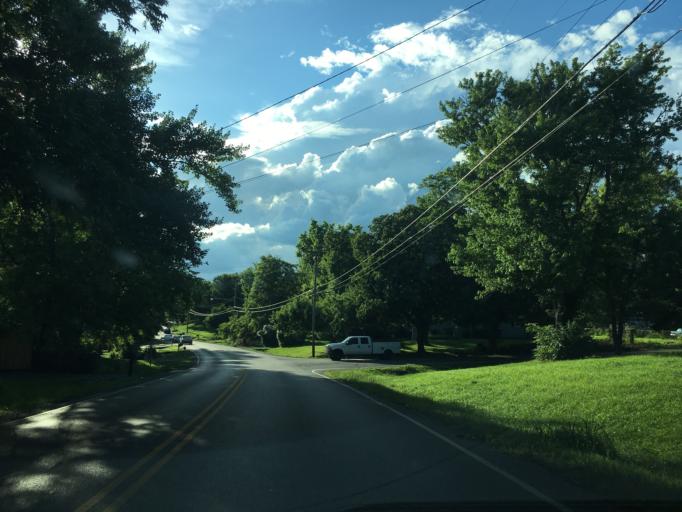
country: US
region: Tennessee
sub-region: Davidson County
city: Oak Hill
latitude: 36.0650
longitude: -86.7267
